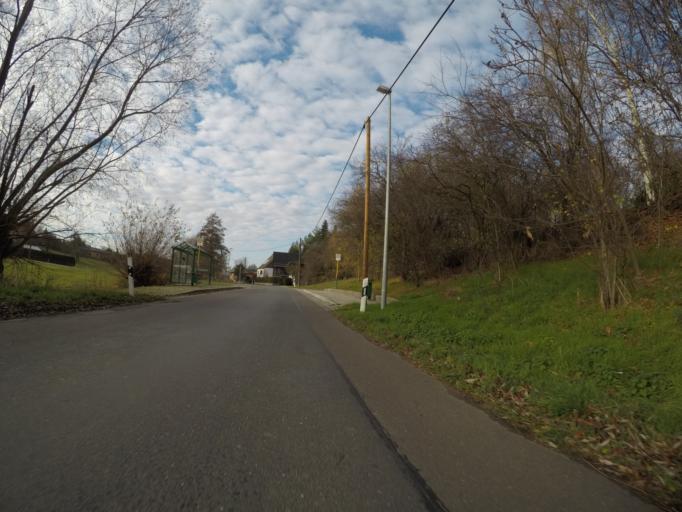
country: DE
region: Thuringia
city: Ponitz
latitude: 50.8569
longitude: 12.3971
